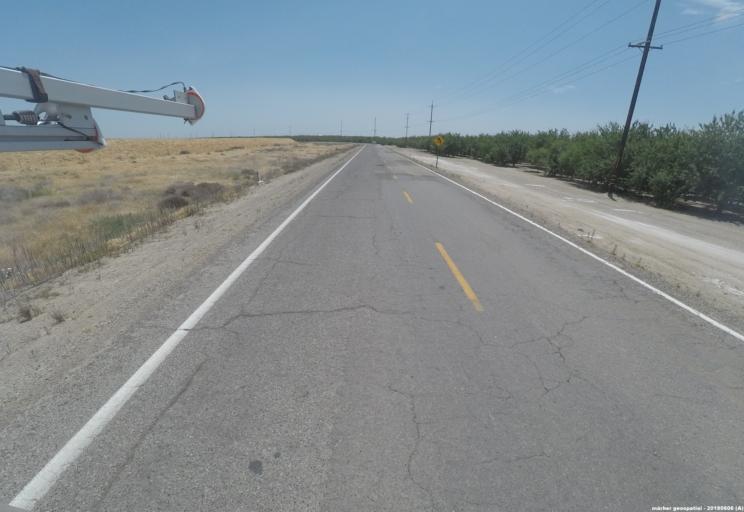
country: US
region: California
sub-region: Fresno County
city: Mendota
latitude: 36.8185
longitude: -120.3044
